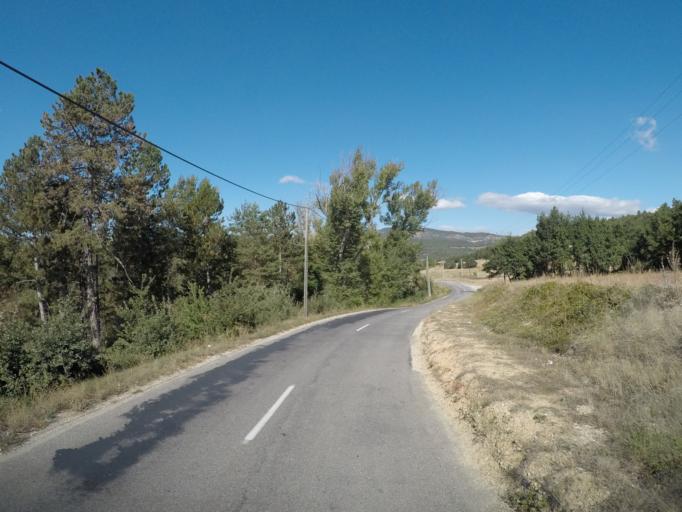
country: FR
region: Provence-Alpes-Cote d'Azur
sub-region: Departement des Alpes-de-Haute-Provence
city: Mallemoisson
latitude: 44.0431
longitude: 6.1679
